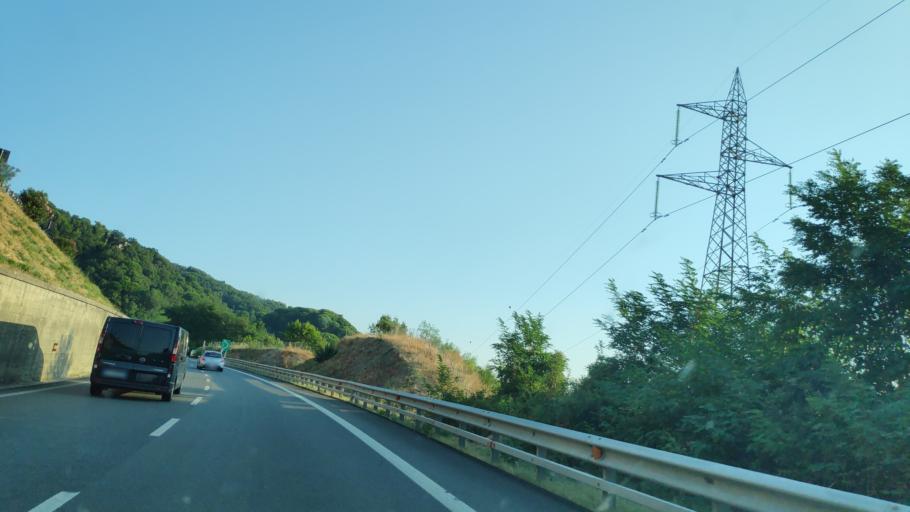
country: IT
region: Calabria
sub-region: Provincia di Cosenza
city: Belsito
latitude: 39.1675
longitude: 16.2935
